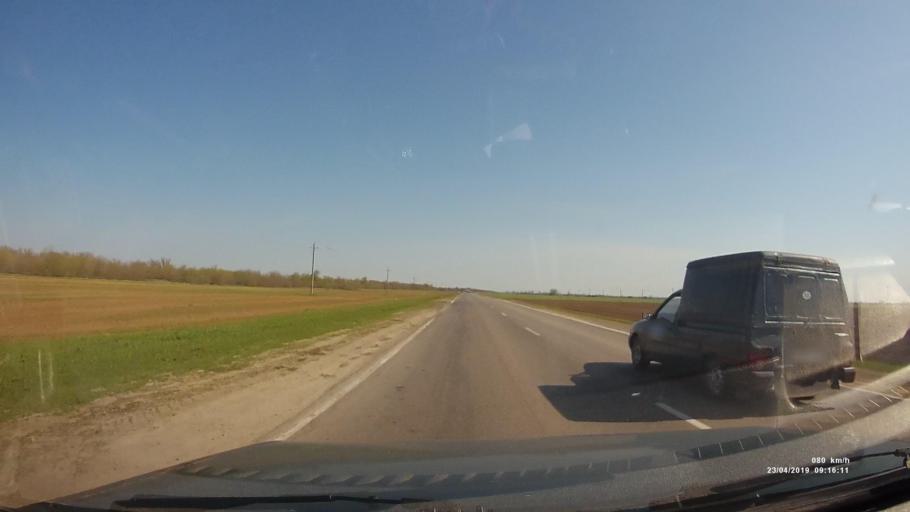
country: RU
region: Rostov
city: Proletarsk
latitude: 46.6374
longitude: 41.6690
